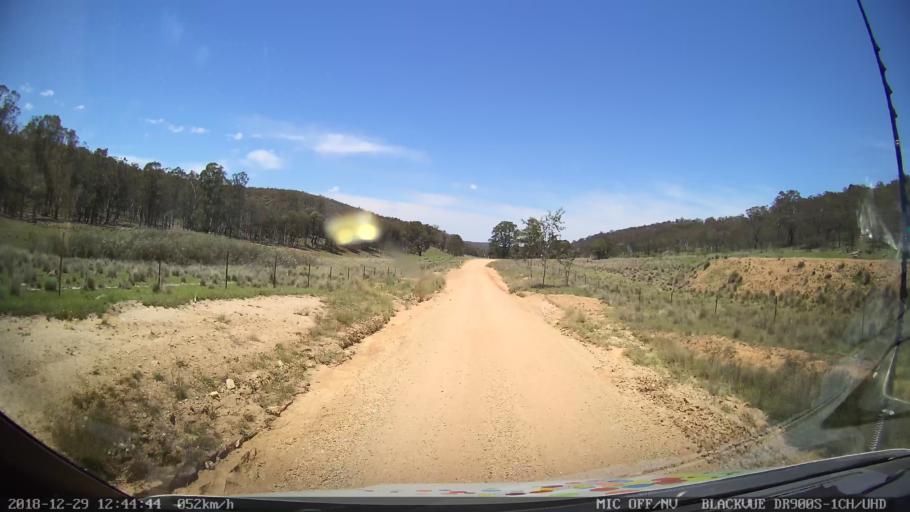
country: AU
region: Australian Capital Territory
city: Macarthur
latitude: -35.6297
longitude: 149.2158
